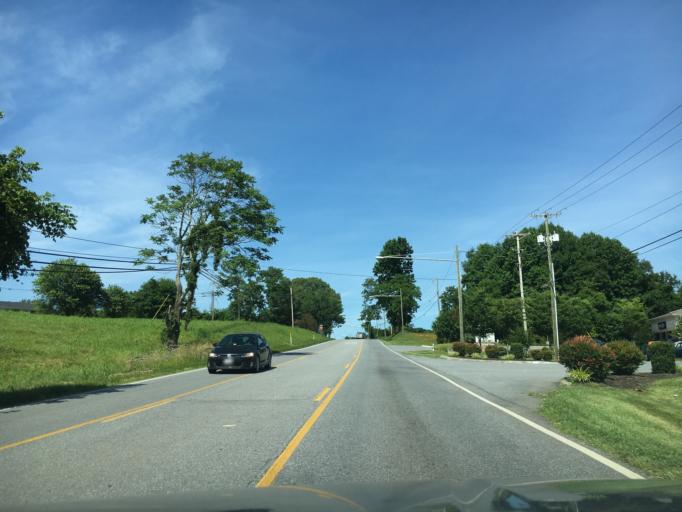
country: US
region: Virginia
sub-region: City of Lynchburg
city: West Lynchburg
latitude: 37.3989
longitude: -79.2129
